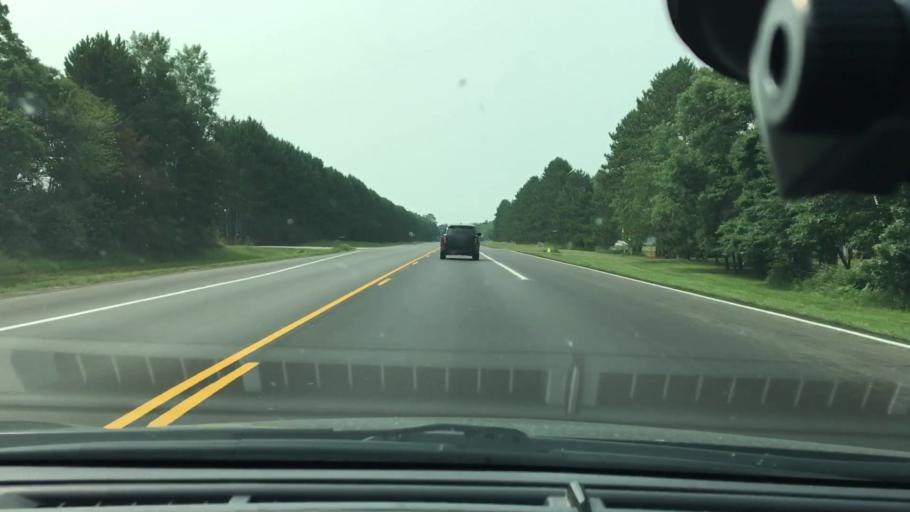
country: US
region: Minnesota
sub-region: Crow Wing County
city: Brainerd
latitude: 46.4323
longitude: -94.1738
